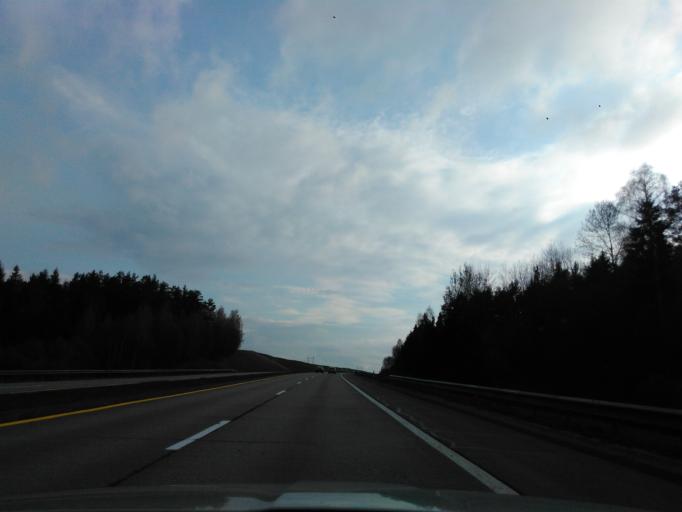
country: BY
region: Minsk
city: Astrashytski Haradok
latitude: 54.1057
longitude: 27.7988
